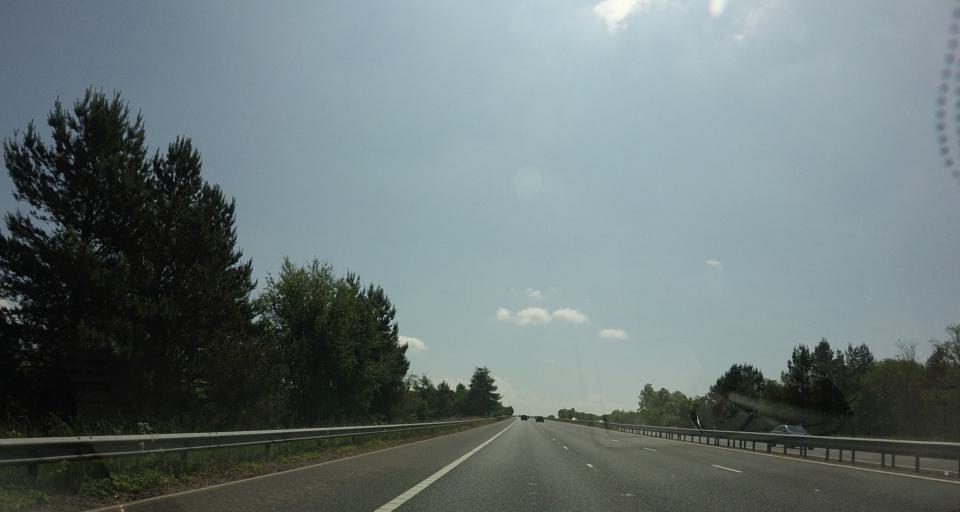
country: GB
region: Scotland
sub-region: Dumfries and Galloway
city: Lockerbie
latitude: 55.0880
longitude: -3.3188
